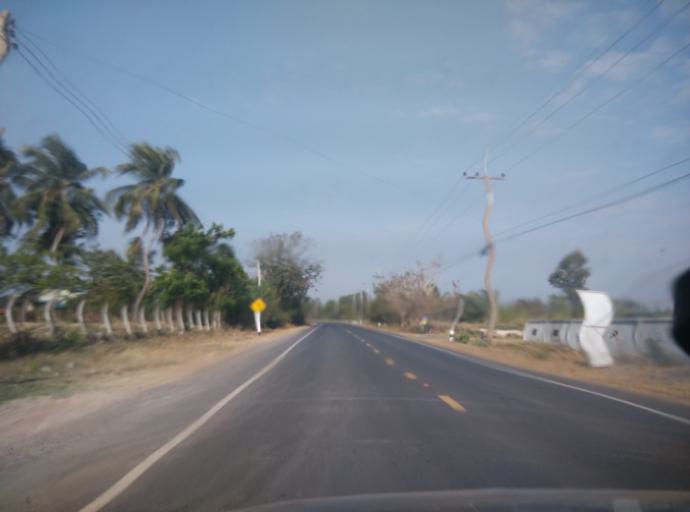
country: TH
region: Sisaket
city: Si Sa Ket
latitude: 15.1161
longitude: 104.2610
